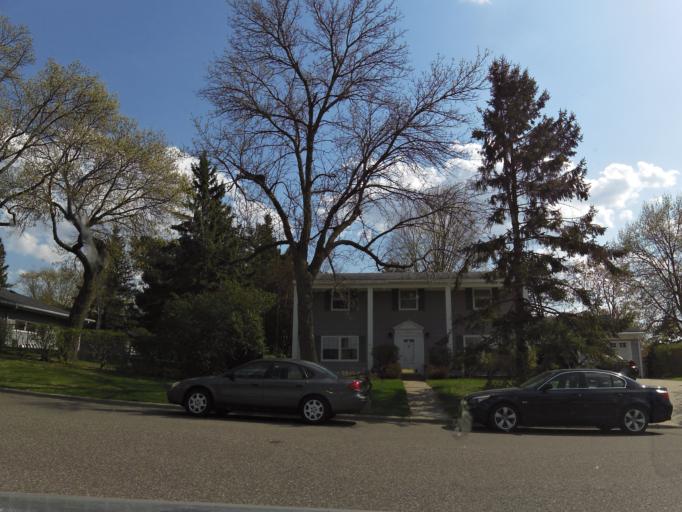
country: US
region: Minnesota
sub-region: Washington County
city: Stillwater
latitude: 45.0430
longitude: -92.8142
